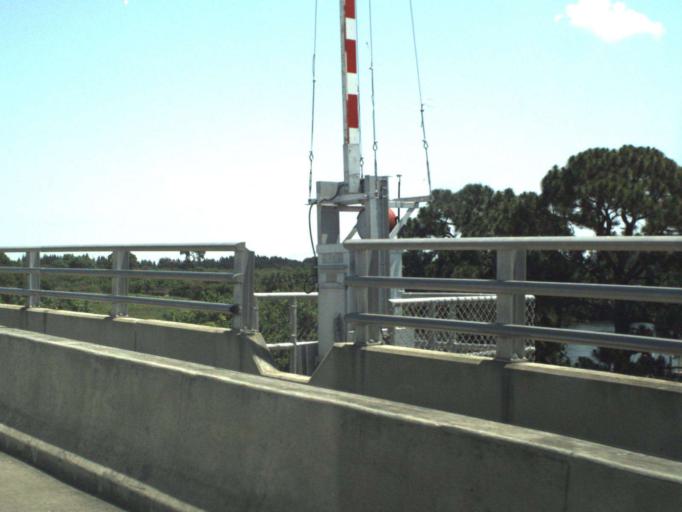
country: US
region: Florida
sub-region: Brevard County
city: Cocoa
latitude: 28.4071
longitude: -80.7057
